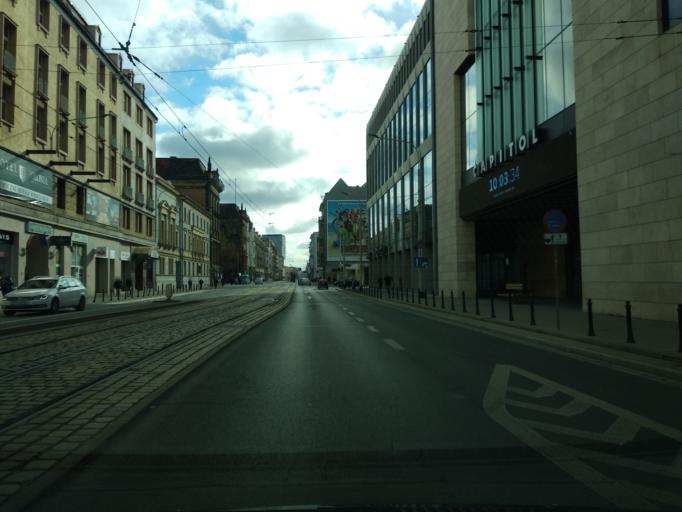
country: PL
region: Lower Silesian Voivodeship
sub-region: Powiat wroclawski
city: Wroclaw
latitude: 51.1011
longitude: 17.0301
